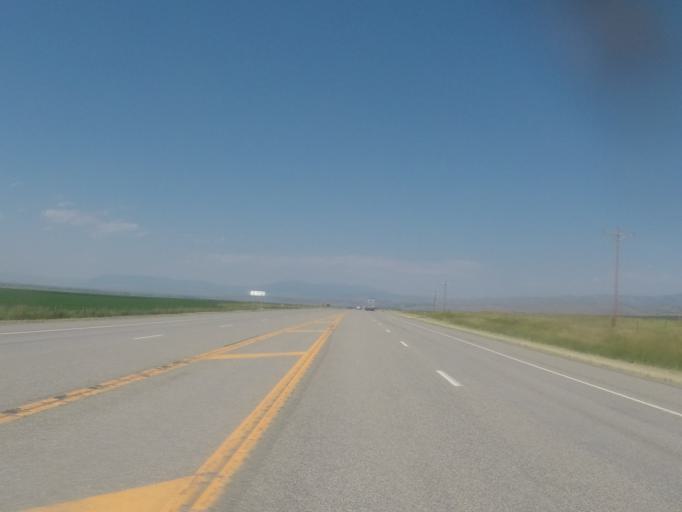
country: US
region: Montana
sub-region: Broadwater County
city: Townsend
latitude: 46.1098
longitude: -111.5084
